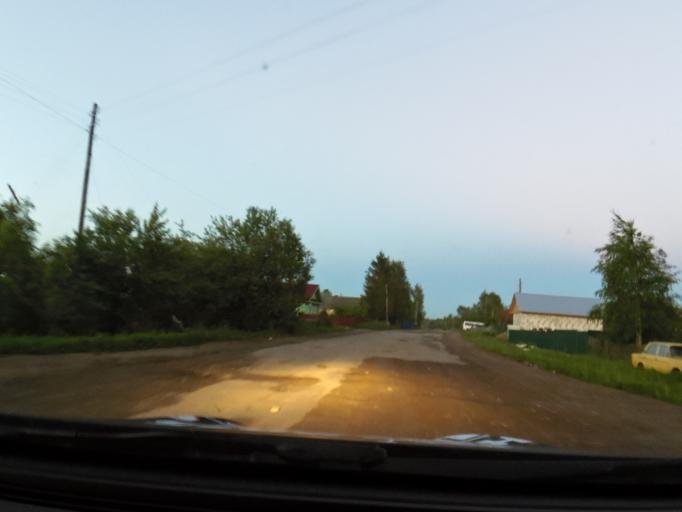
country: RU
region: Vologda
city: Vytegra
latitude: 60.9939
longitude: 36.3440
